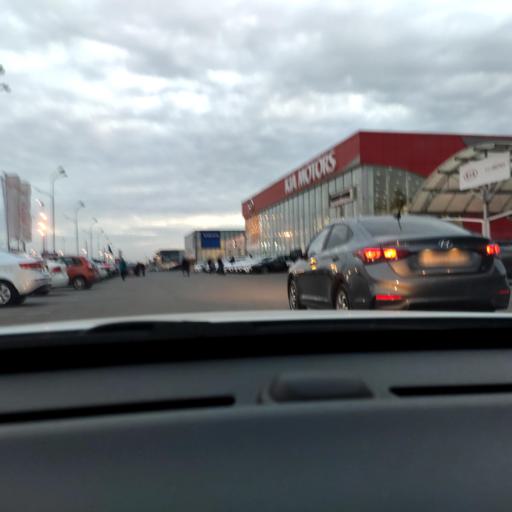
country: RU
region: Voronezj
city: Somovo
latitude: 51.6644
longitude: 39.3002
